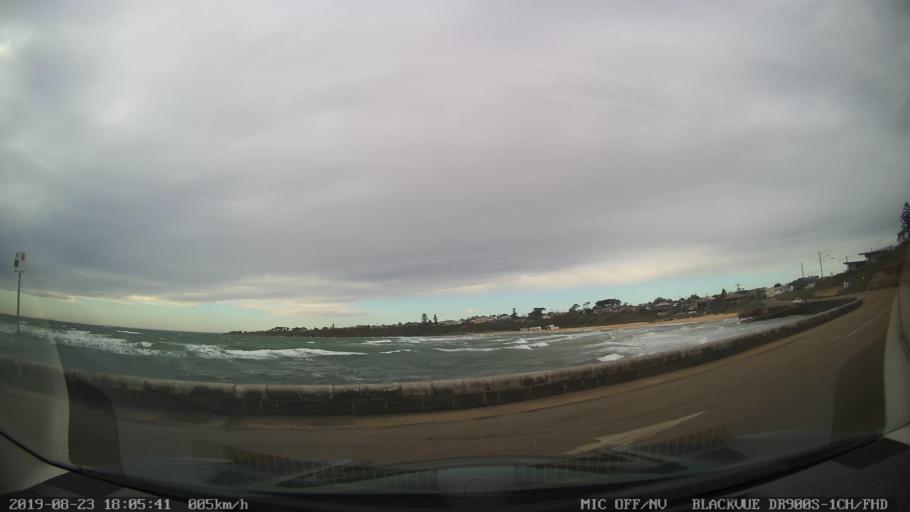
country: AU
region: Victoria
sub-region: Mornington Peninsula
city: Mornington
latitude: -38.2255
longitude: 145.0266
